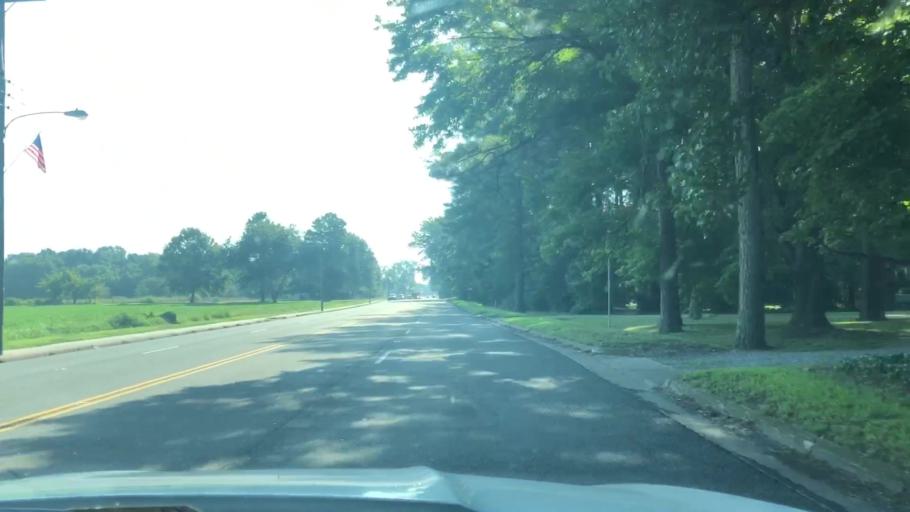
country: US
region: Virginia
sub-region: Richmond County
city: Warsaw
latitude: 37.9589
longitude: -76.7689
